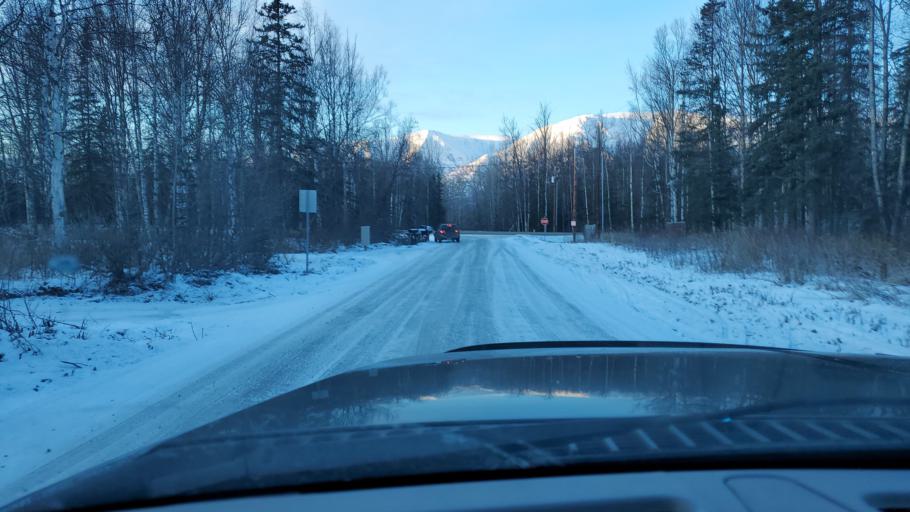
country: US
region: Alaska
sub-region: Matanuska-Susitna Borough
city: Lakes
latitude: 61.6680
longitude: -149.2951
